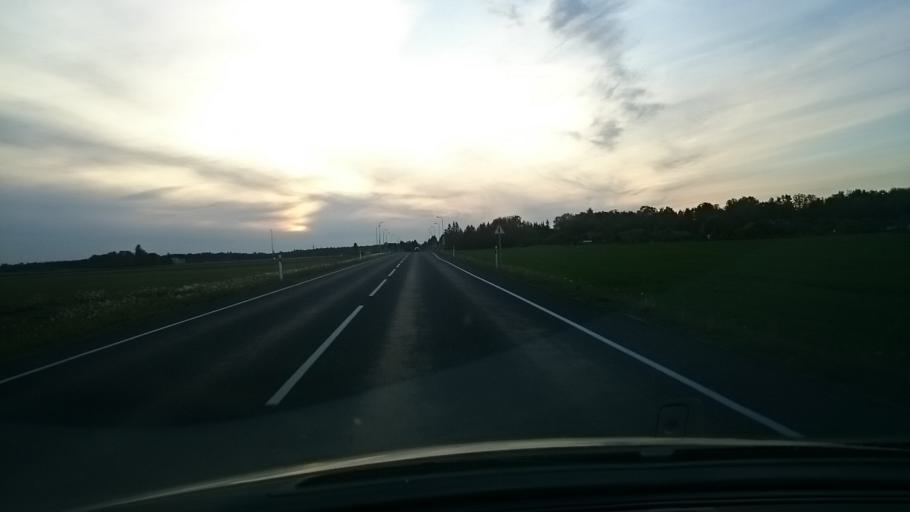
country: EE
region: Viljandimaa
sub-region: Vohma linn
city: Vohma
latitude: 58.7521
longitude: 25.5658
